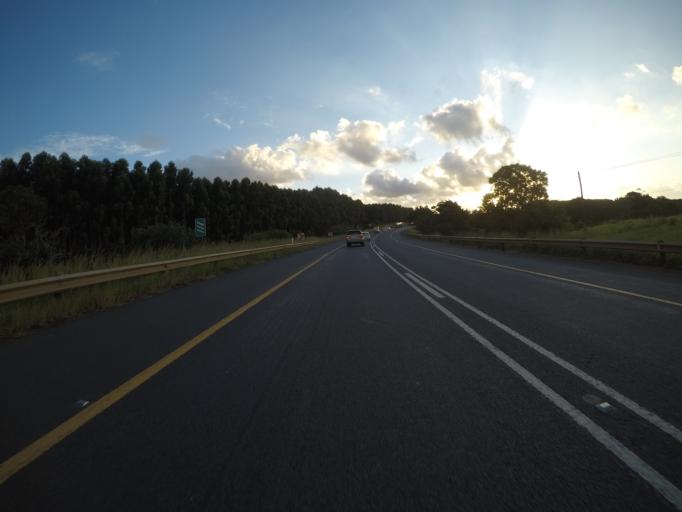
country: ZA
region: KwaZulu-Natal
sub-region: uThungulu District Municipality
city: Richards Bay
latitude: -28.6920
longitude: 32.0362
